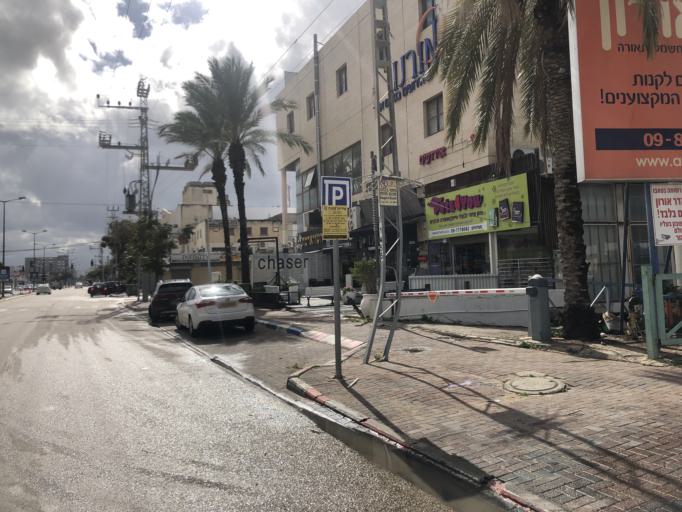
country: IL
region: Central District
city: Bet Yizhaq
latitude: 32.3218
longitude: 34.8744
